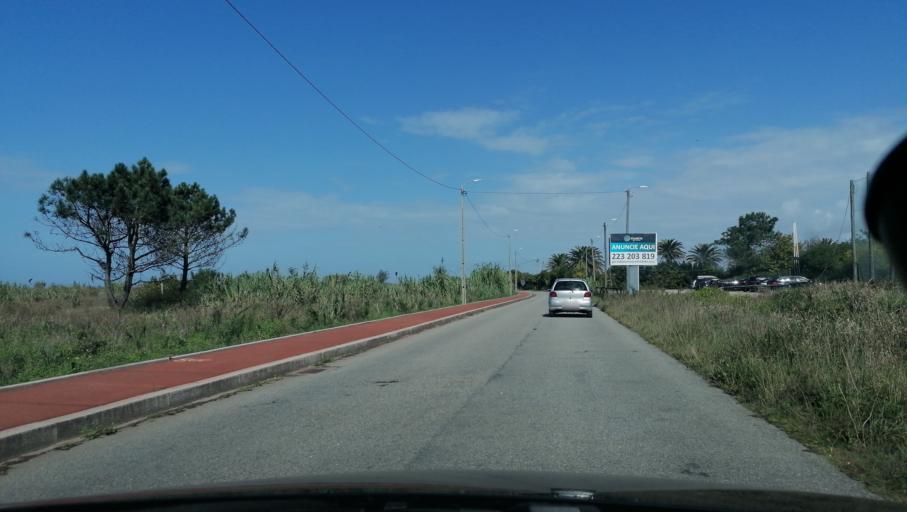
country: PT
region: Aveiro
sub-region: Espinho
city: Silvalde
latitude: 40.9834
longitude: -8.6426
